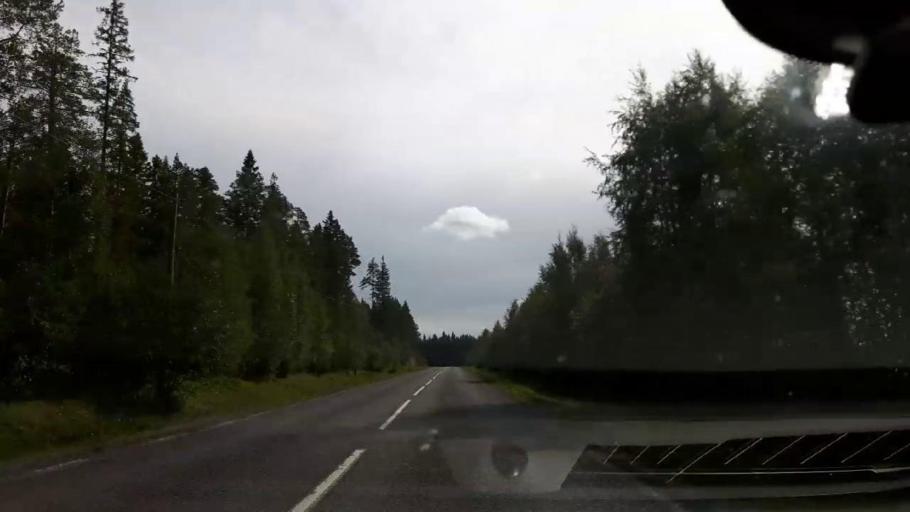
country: SE
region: Jaemtland
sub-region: Ragunda Kommun
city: Hammarstrand
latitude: 63.1427
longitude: 15.8591
